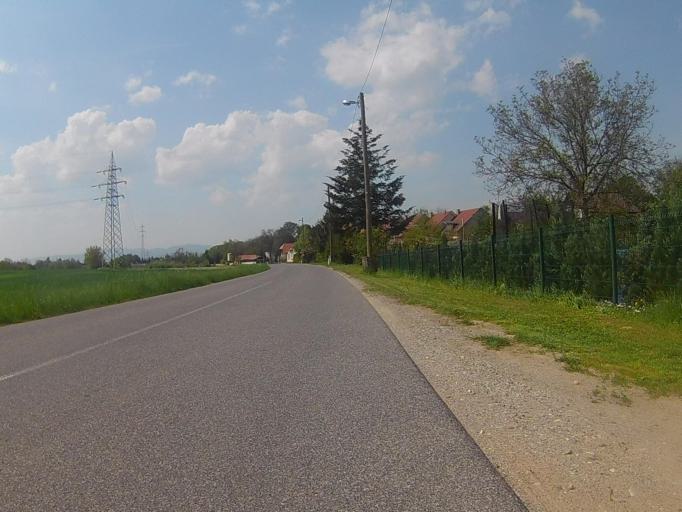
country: SI
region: Duplek
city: Zgornji Duplek
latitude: 46.5487
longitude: 15.6974
